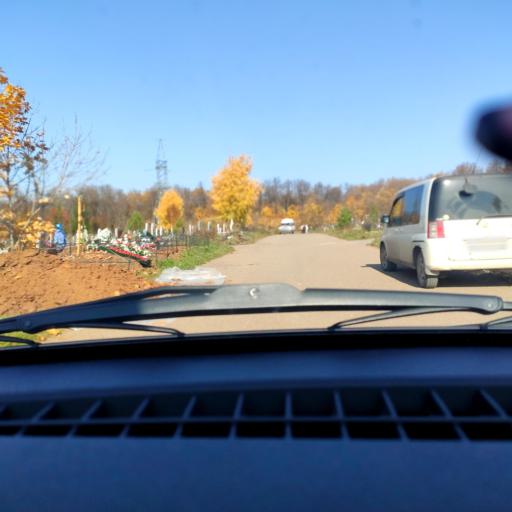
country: RU
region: Bashkortostan
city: Mikhaylovka
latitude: 54.8171
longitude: 55.8664
